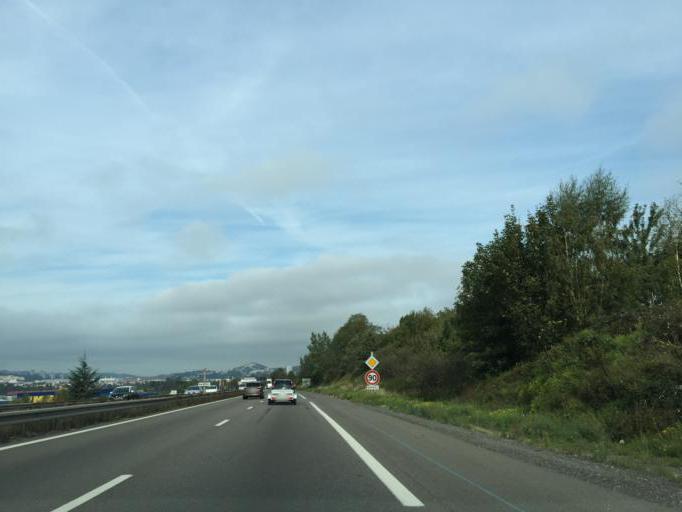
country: FR
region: Rhone-Alpes
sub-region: Departement de la Loire
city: Saint-Jean-Bonnefonds
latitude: 45.4473
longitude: 4.4248
